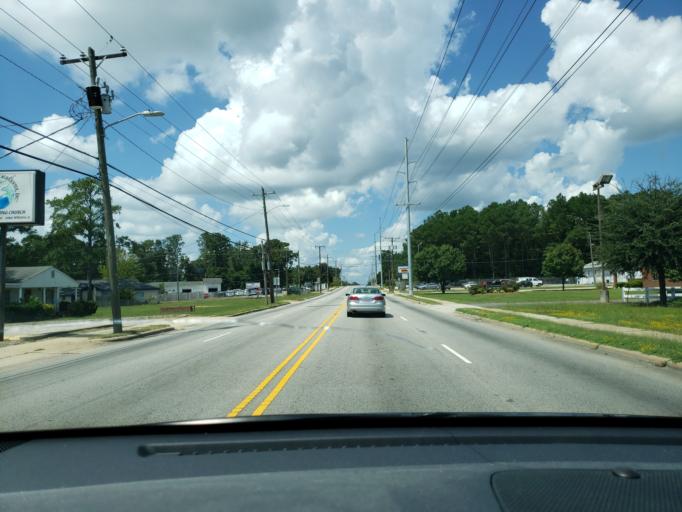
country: US
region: North Carolina
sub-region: Cumberland County
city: Fayetteville
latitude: 35.0922
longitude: -78.9114
